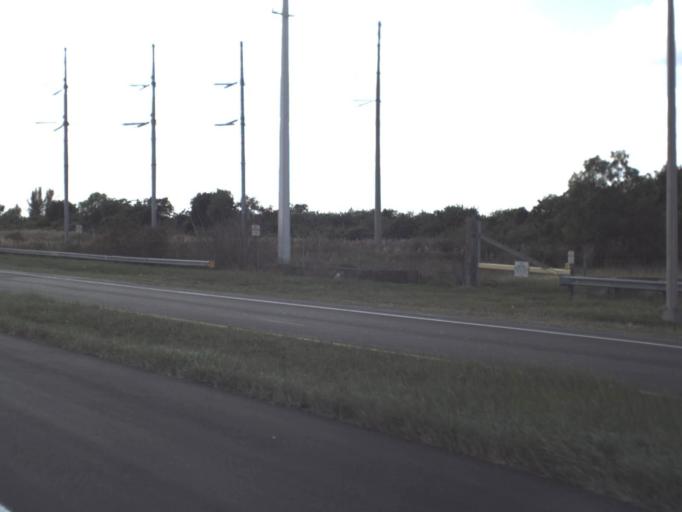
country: US
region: Florida
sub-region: Broward County
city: Coral Springs
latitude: 26.2296
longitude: -80.2964
